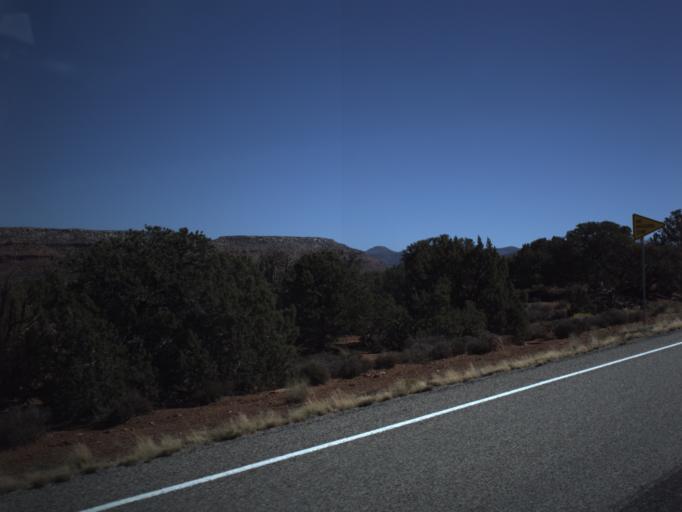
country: US
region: Utah
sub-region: San Juan County
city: Blanding
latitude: 37.6569
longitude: -110.1777
